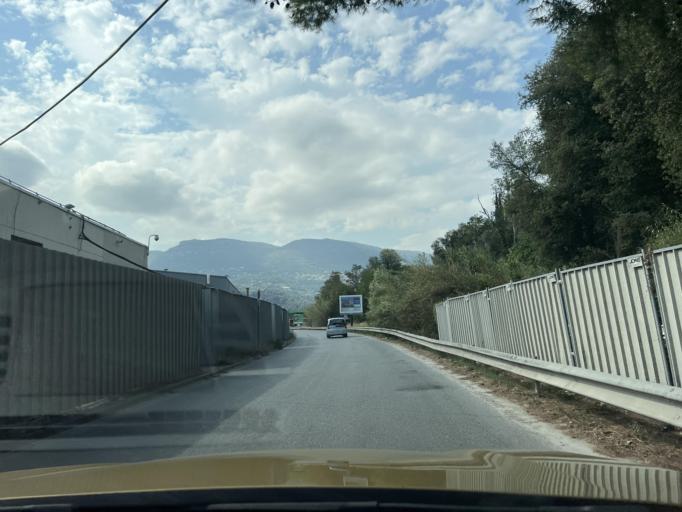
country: FR
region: Provence-Alpes-Cote d'Azur
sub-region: Departement des Alpes-Maritimes
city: Gattieres
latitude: 43.7295
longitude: 7.1899
